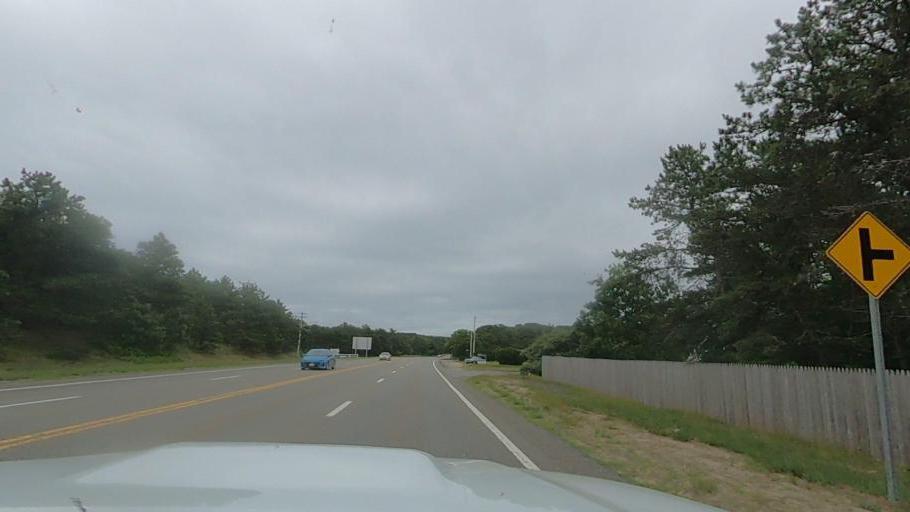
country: US
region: Massachusetts
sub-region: Barnstable County
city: Truro
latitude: 42.0456
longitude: -70.0974
